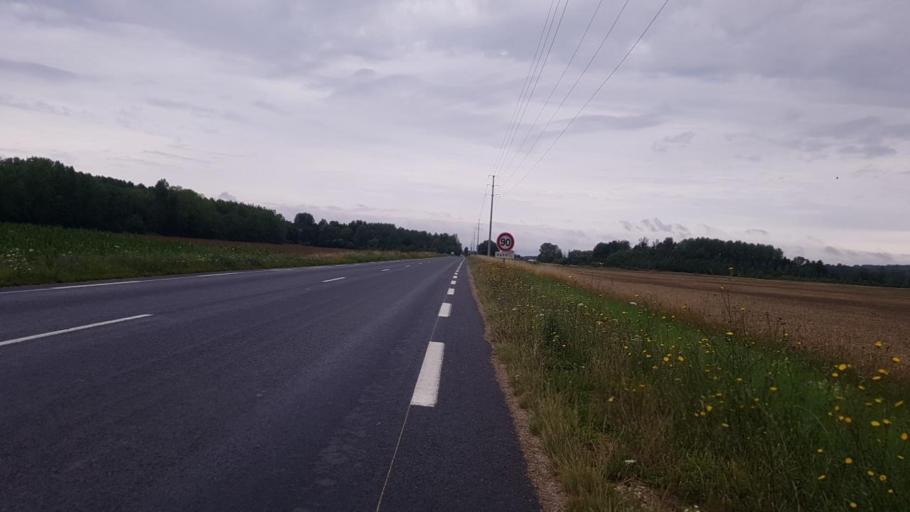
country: FR
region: Champagne-Ardenne
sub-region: Departement de la Marne
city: Vitry-le-Francois
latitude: 48.7409
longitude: 4.6558
